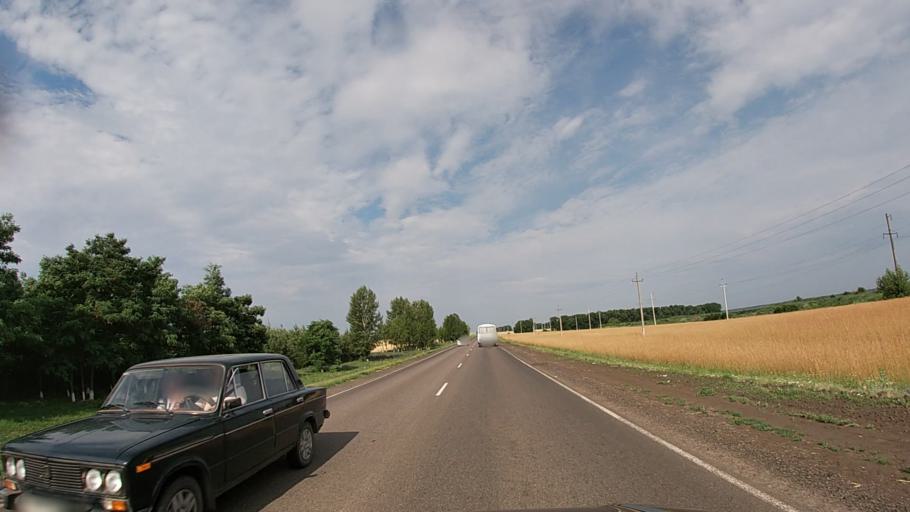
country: RU
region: Belgorod
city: Krasnaya Yaruga
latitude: 50.7980
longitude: 35.6075
